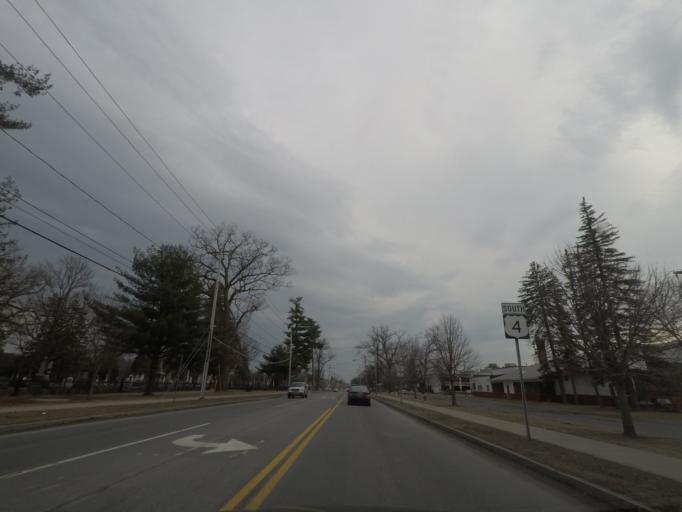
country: US
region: New York
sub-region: Washington County
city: Hudson Falls
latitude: 43.2880
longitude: -73.5867
